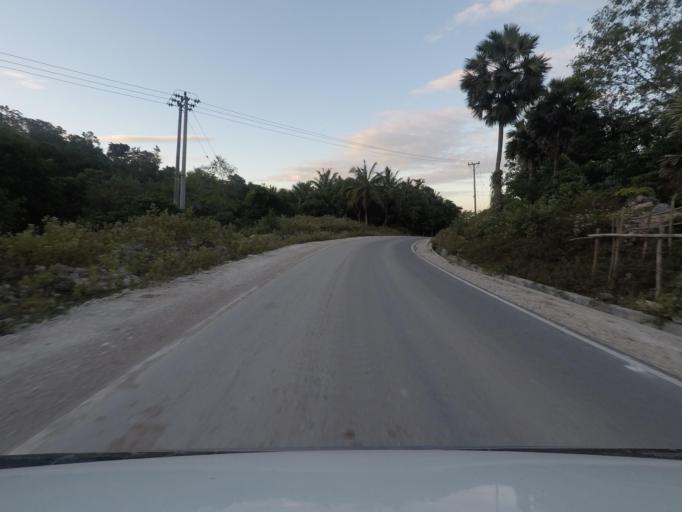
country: TL
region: Lautem
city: Lospalos
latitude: -8.3984
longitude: 127.2580
